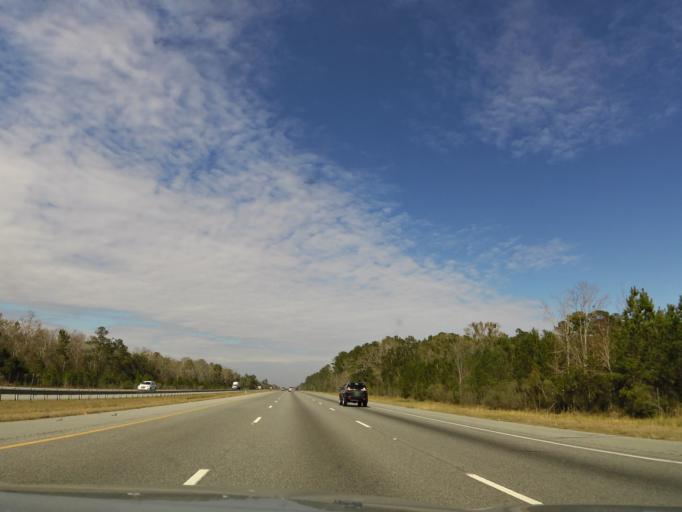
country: US
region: Georgia
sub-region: McIntosh County
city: Darien
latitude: 31.4999
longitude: -81.4464
